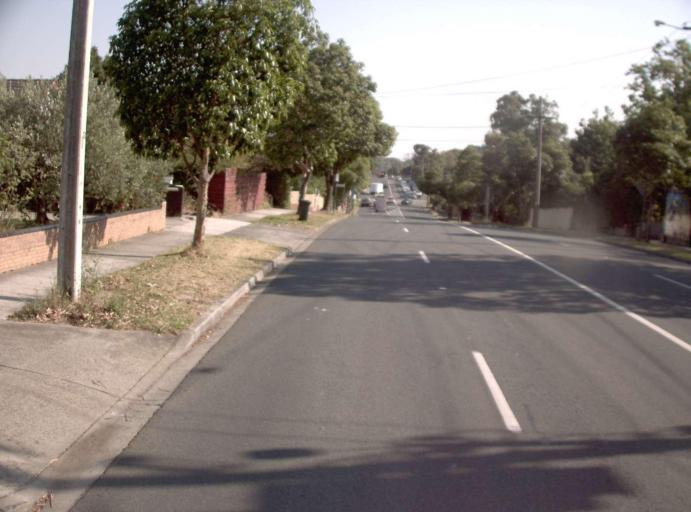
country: AU
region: Victoria
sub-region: Whitehorse
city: Burwood
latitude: -37.8526
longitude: 145.1195
